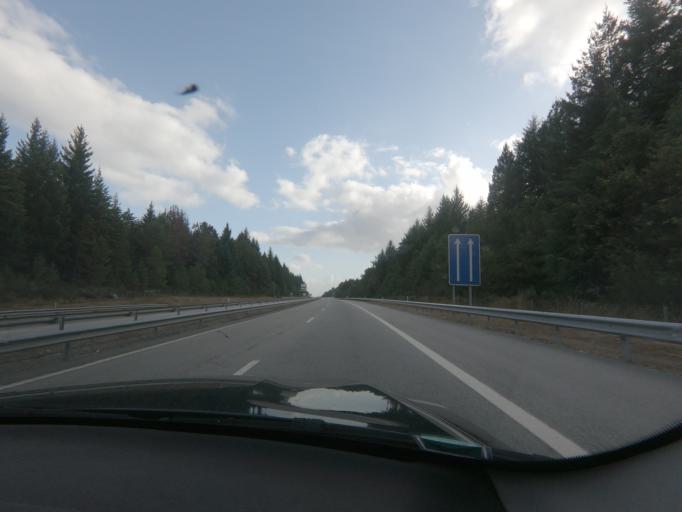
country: PT
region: Viseu
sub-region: Viseu
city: Abraveses
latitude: 40.6926
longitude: -7.9643
